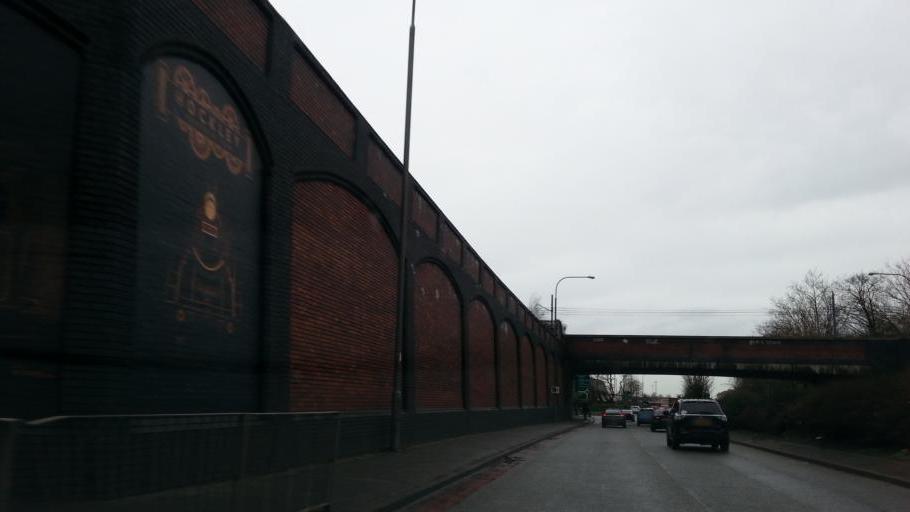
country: GB
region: England
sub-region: City and Borough of Birmingham
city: Hockley
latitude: 52.4896
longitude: -1.9169
